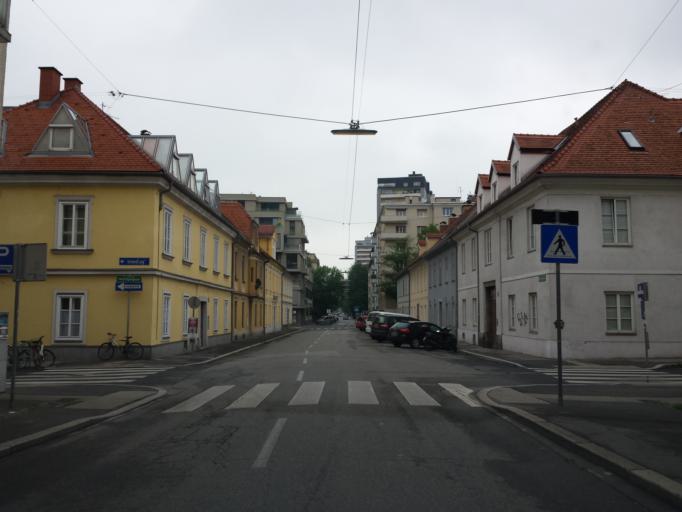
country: AT
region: Styria
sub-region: Graz Stadt
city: Graz
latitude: 47.0797
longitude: 15.4371
